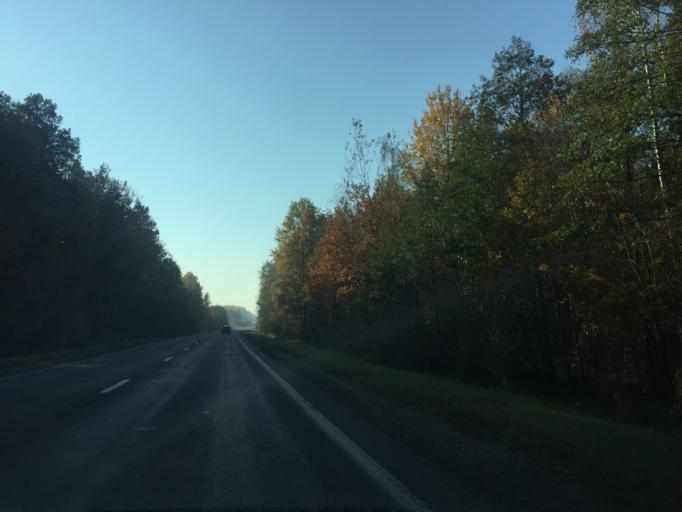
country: BY
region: Gomel
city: Kastsyukowka
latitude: 52.4268
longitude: 30.8279
